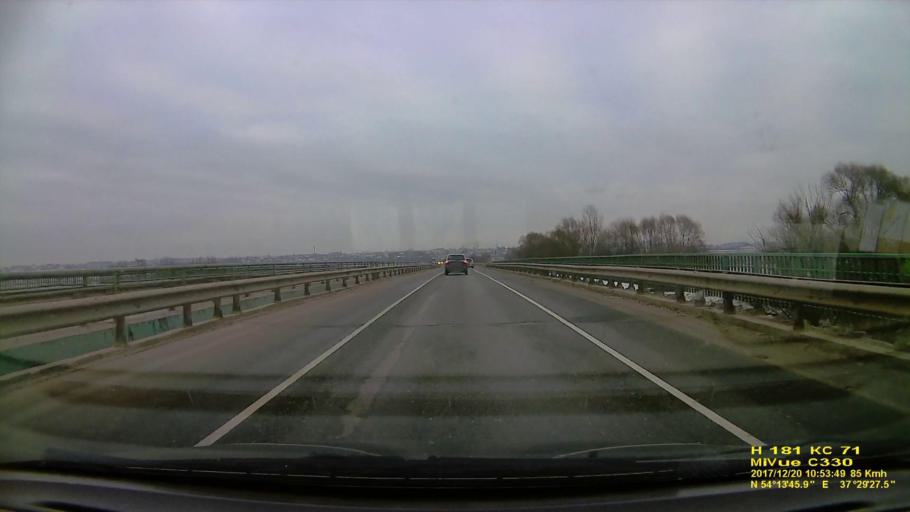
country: RU
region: Tula
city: Barsuki
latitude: 54.2295
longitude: 37.4912
